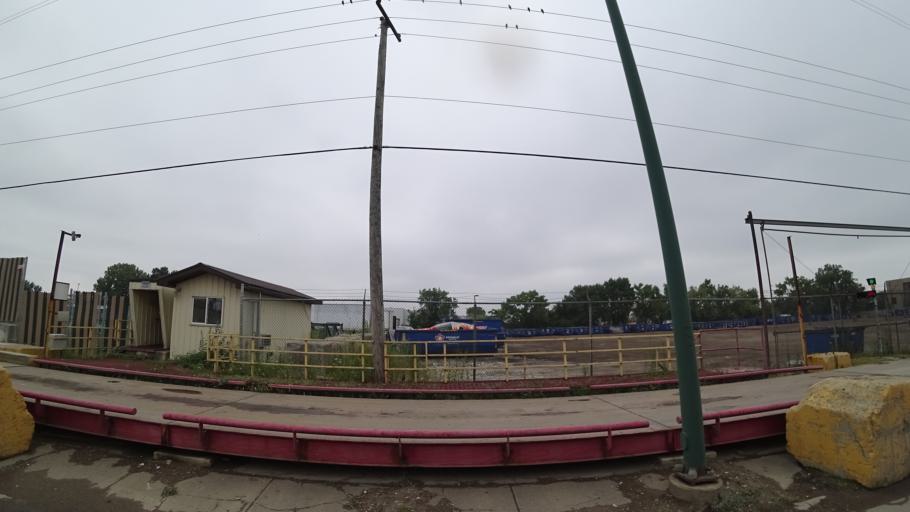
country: US
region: Illinois
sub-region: Cook County
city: Chicago
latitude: 41.8509
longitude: -87.6636
